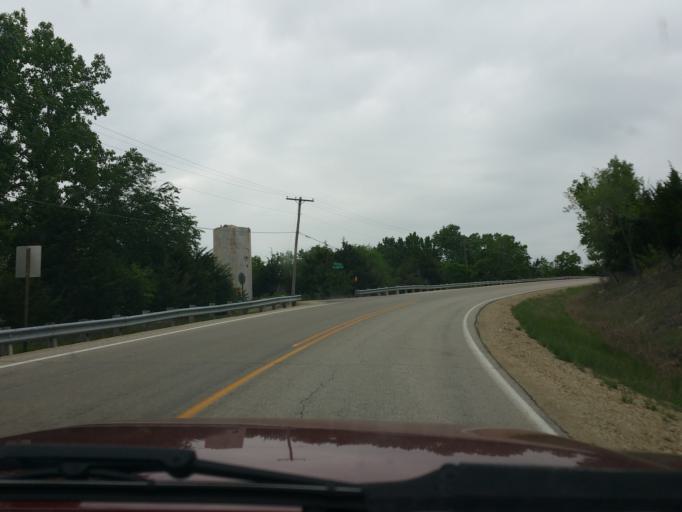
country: US
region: Kansas
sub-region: Riley County
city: Manhattan
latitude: 39.2532
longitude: -96.6129
